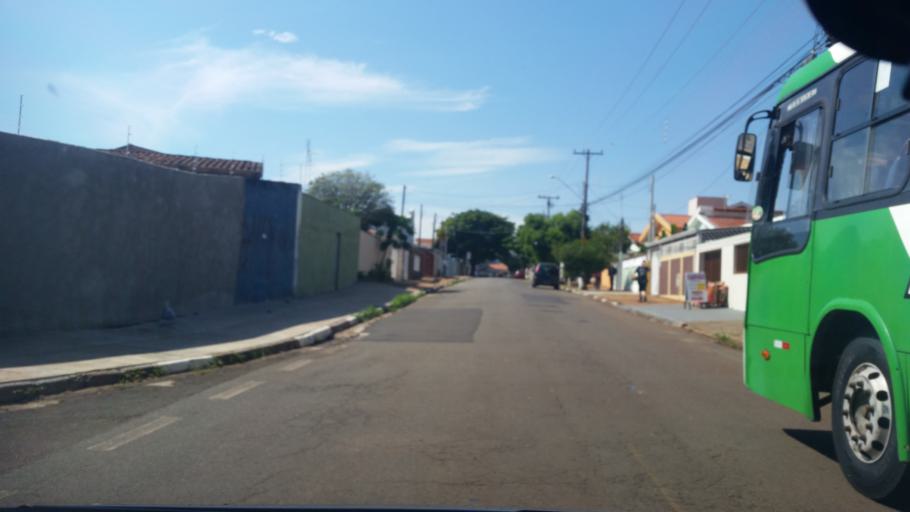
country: BR
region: Sao Paulo
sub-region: Campinas
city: Campinas
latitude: -22.8691
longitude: -47.0651
